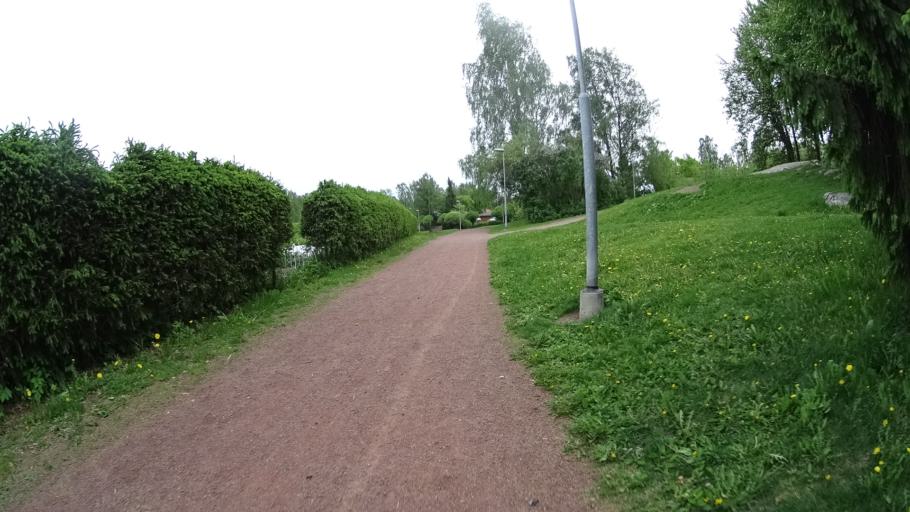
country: FI
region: Uusimaa
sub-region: Helsinki
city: Vantaa
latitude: 60.2736
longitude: 25.0596
